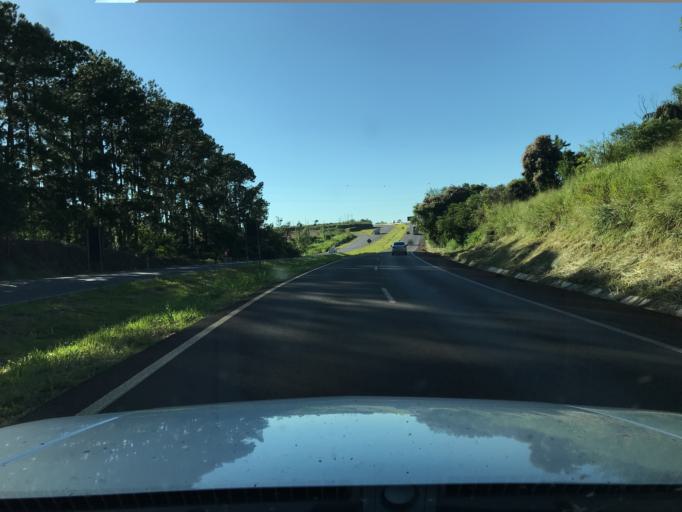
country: BR
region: Parana
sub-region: Cascavel
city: Cascavel
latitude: -24.8934
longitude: -53.5366
